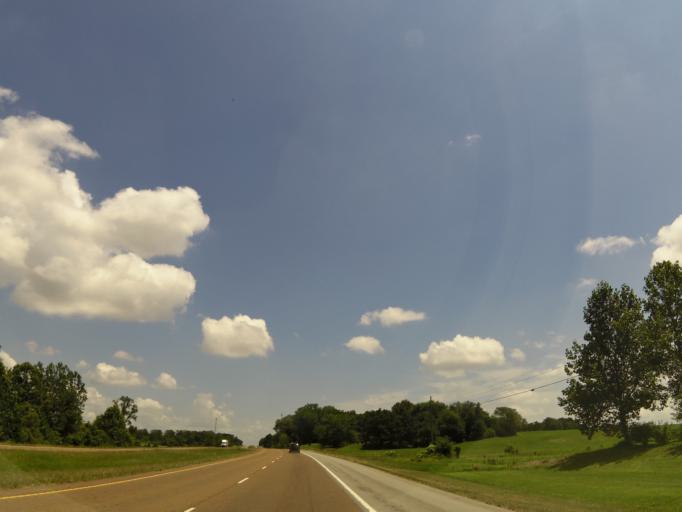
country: US
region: Tennessee
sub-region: Lauderdale County
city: Halls
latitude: 35.9179
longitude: -89.2735
